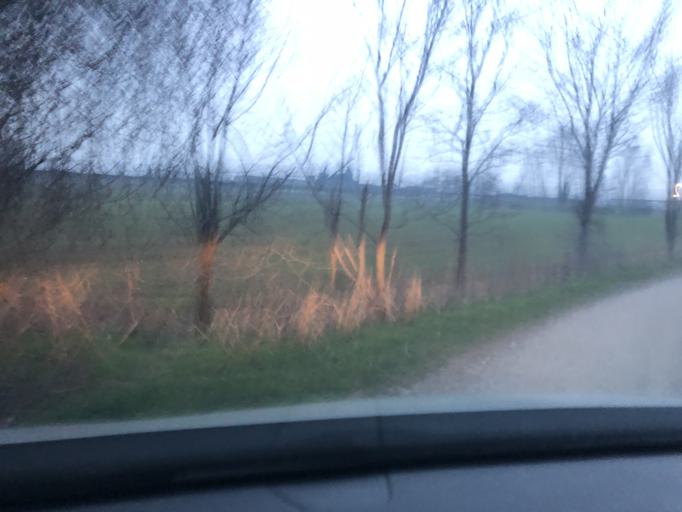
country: IT
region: Veneto
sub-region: Provincia di Verona
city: Sommacampagna
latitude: 45.4047
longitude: 10.8670
